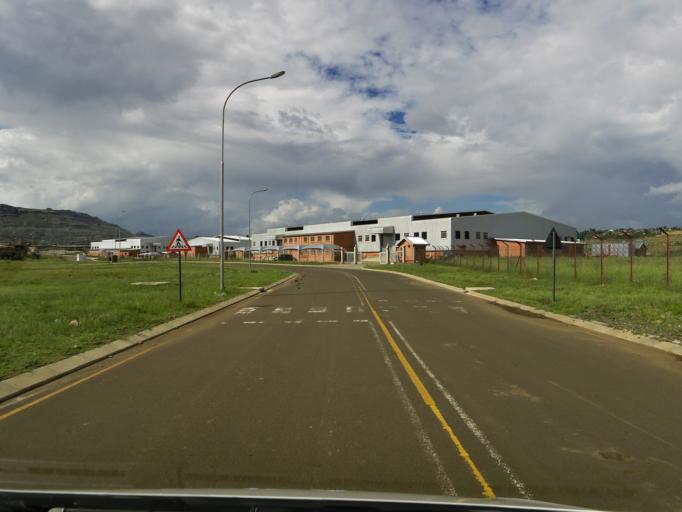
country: LS
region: Maseru
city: Maseru
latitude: -29.3825
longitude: 27.4867
